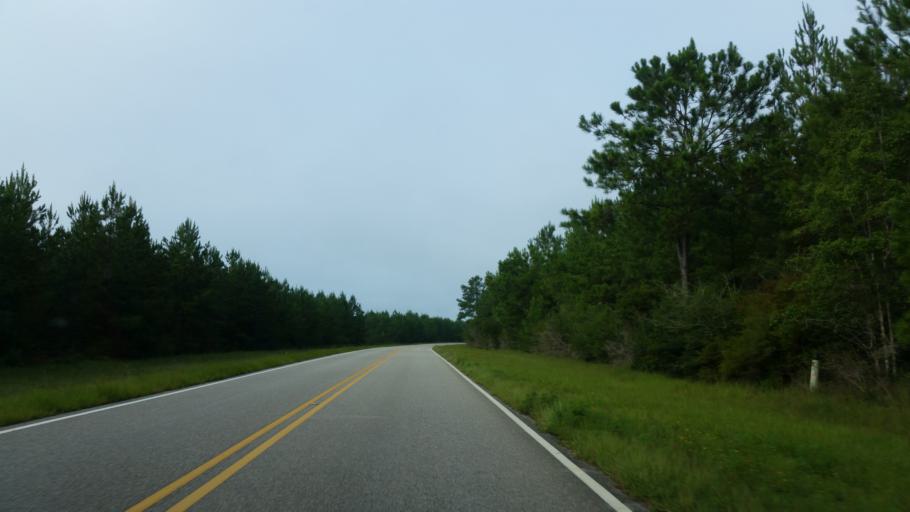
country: US
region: Florida
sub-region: Escambia County
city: Cantonment
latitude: 30.6796
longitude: -87.5321
